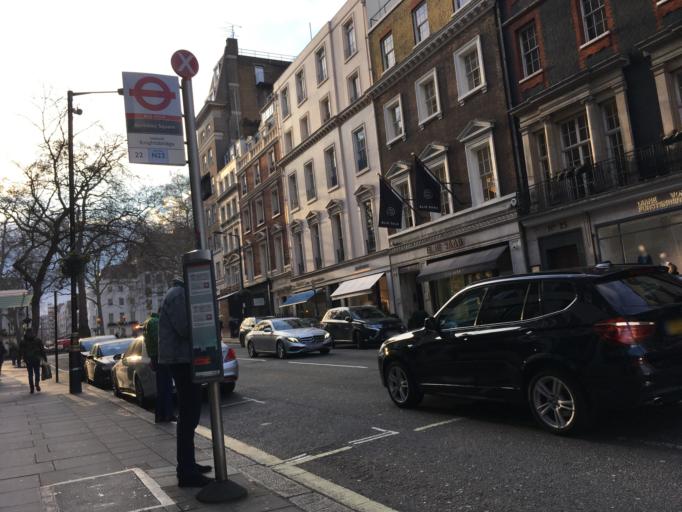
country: GB
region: England
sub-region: Greater London
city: London
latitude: 51.5105
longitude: -0.1449
